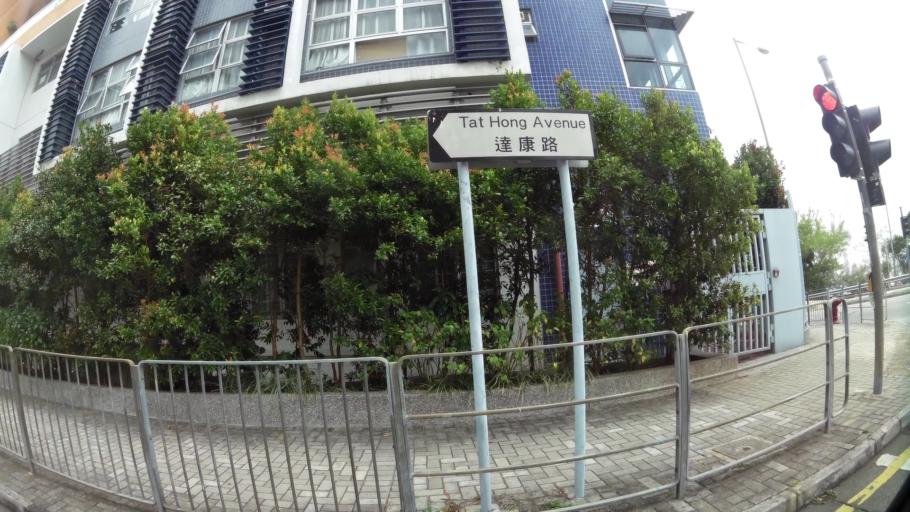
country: HK
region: Sham Shui Po
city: Sham Shui Po
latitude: 22.3399
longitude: 114.1690
